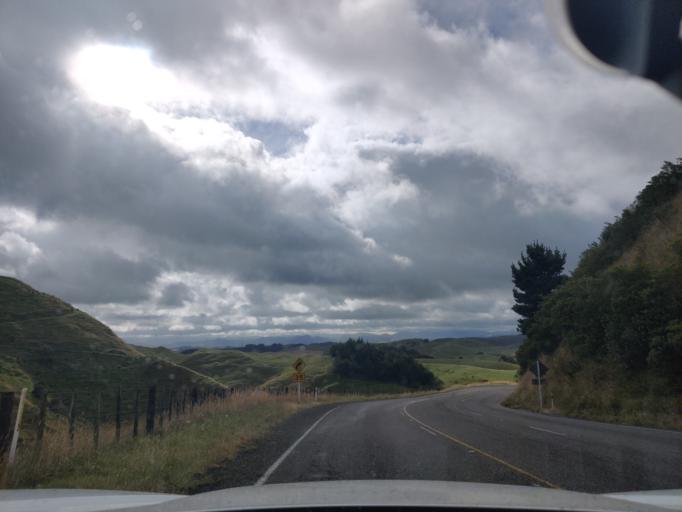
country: NZ
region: Manawatu-Wanganui
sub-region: Palmerston North City
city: Palmerston North
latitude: -40.4183
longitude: 175.7388
